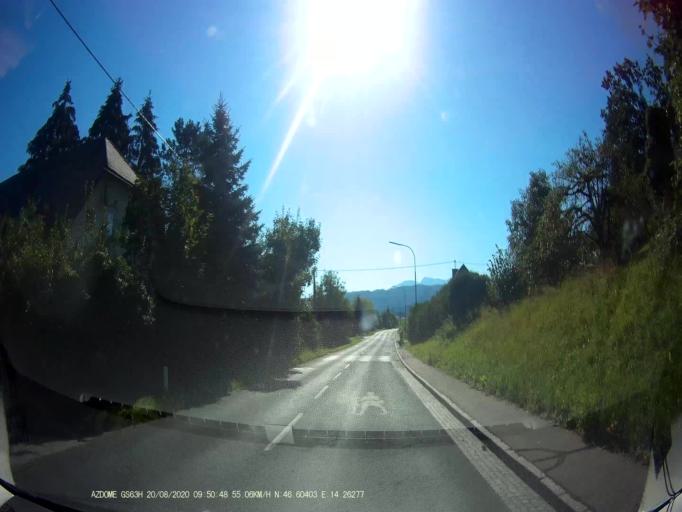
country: AT
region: Carinthia
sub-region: Klagenfurt am Woerthersee
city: Klagenfurt am Woerthersee
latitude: 46.6040
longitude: 14.2630
